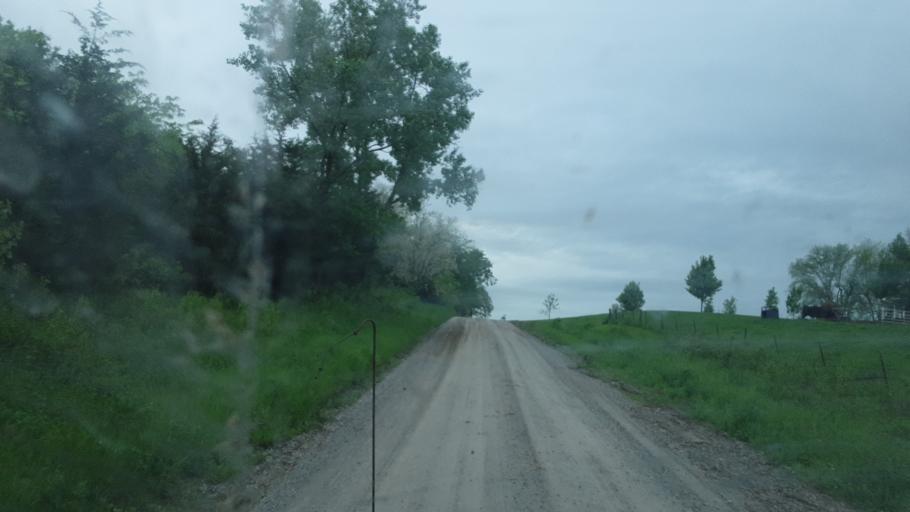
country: US
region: Missouri
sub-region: Clark County
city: Kahoka
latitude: 40.4390
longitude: -91.6156
